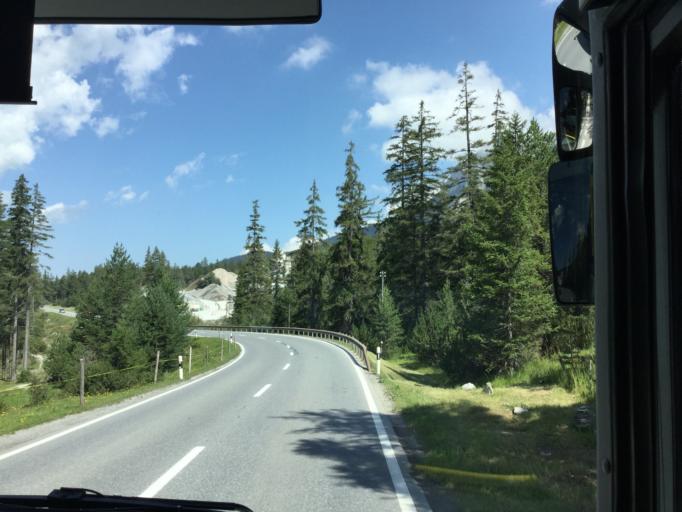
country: CH
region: Grisons
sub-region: Albula District
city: Tiefencastel
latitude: 46.7052
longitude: 9.5603
